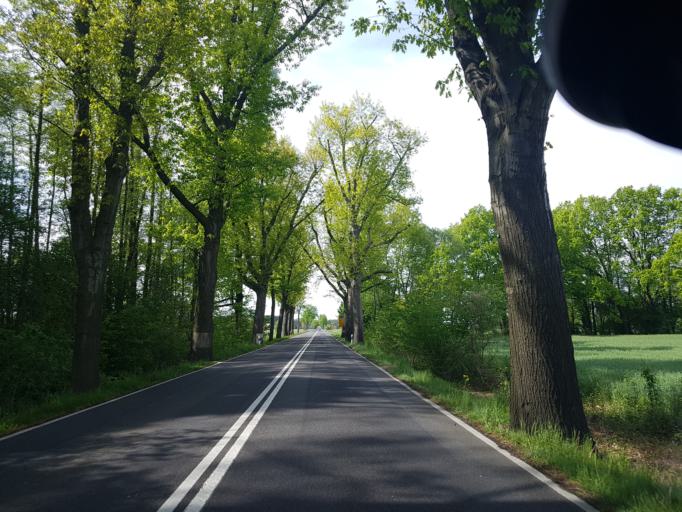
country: DE
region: Saxony
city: Gross Duben
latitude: 51.6774
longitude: 14.5142
